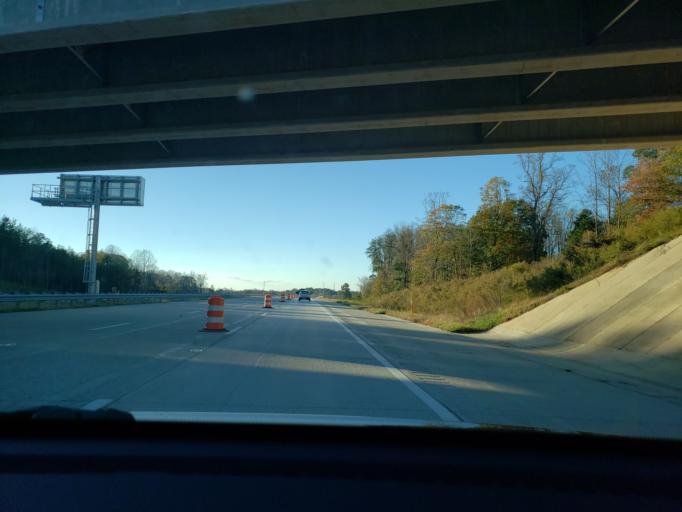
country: US
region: North Carolina
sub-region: Forsyth County
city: Walkertown
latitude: 36.1412
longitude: -80.1462
